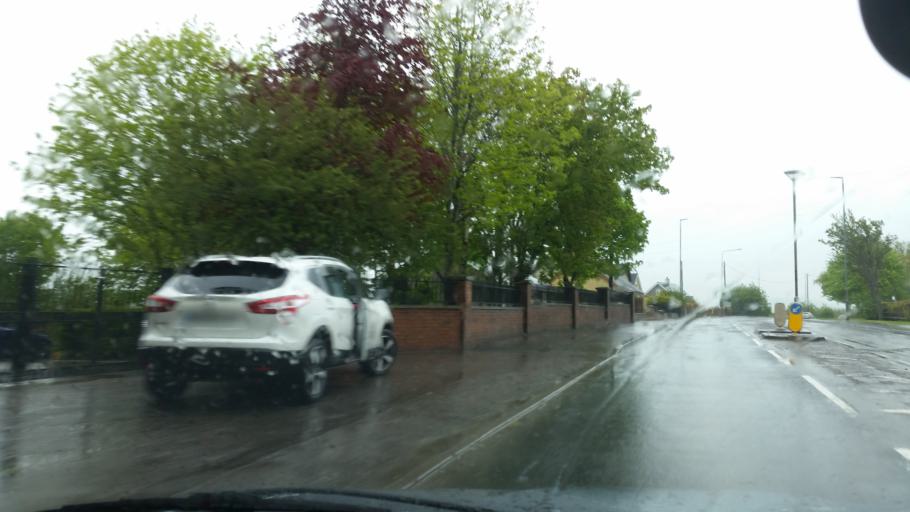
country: GB
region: Northern Ireland
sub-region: Strabane District
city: Strabane
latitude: 54.8407
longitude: -7.4533
